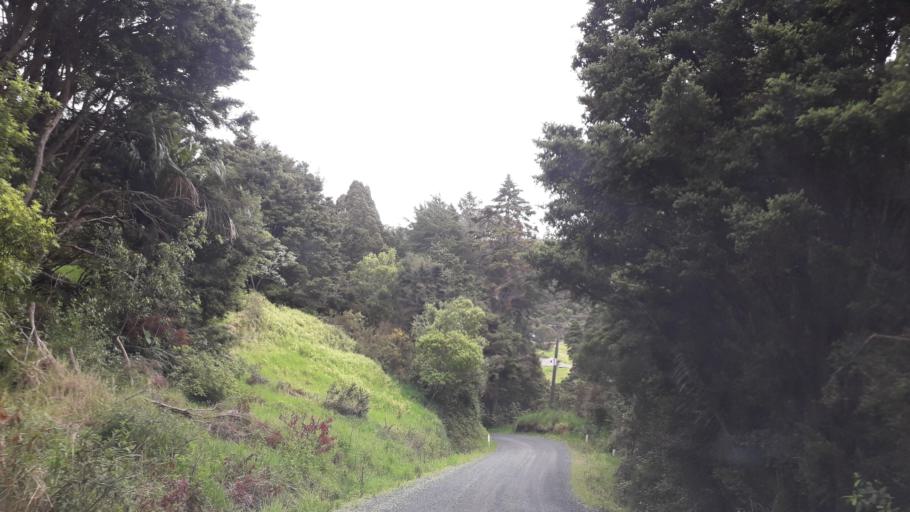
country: NZ
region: Northland
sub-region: Far North District
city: Taipa
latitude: -35.0846
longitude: 173.5520
